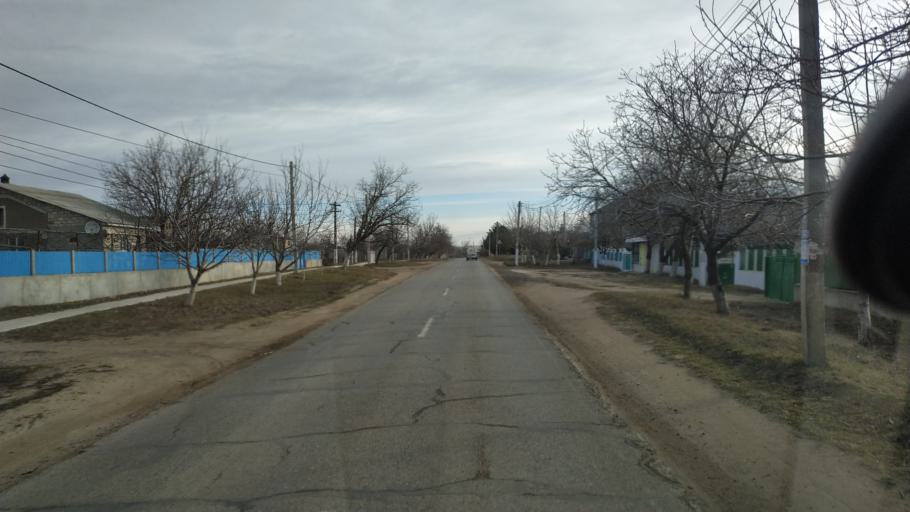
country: MD
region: Criuleni
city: Criuleni
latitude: 47.1600
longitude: 29.1148
